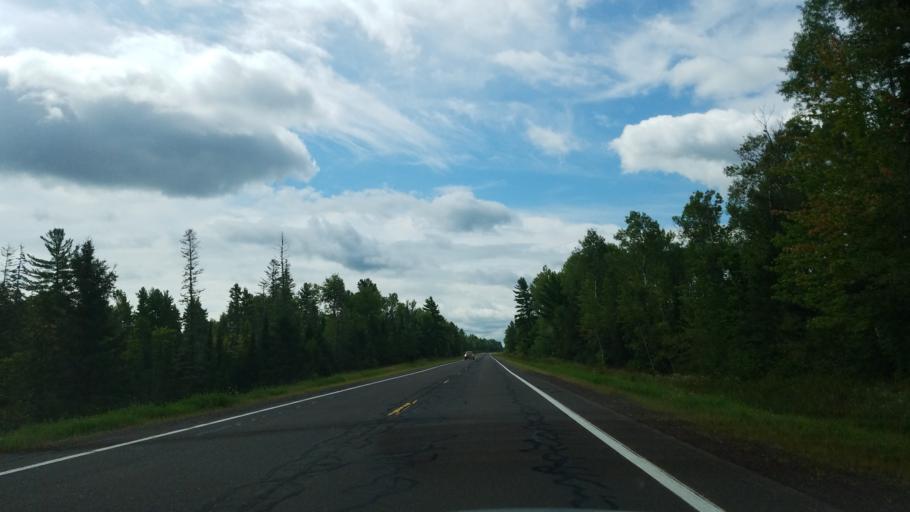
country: US
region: Michigan
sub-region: Ontonagon County
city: Ontonagon
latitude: 46.6579
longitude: -89.1726
